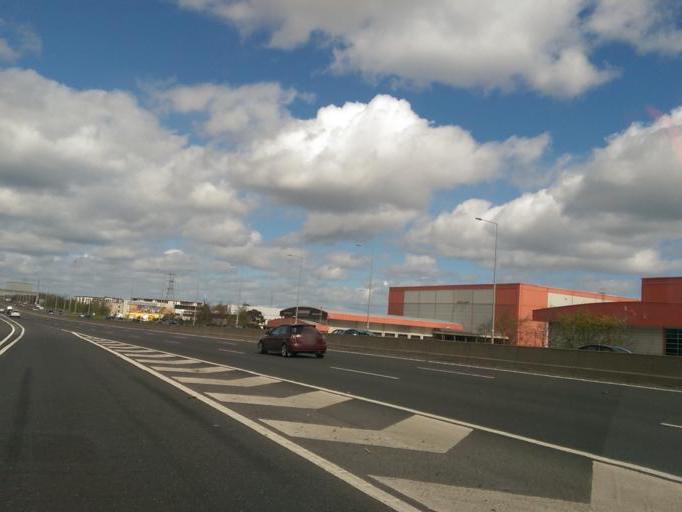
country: IE
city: Cherry Orchard
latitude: 53.3228
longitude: -6.3722
